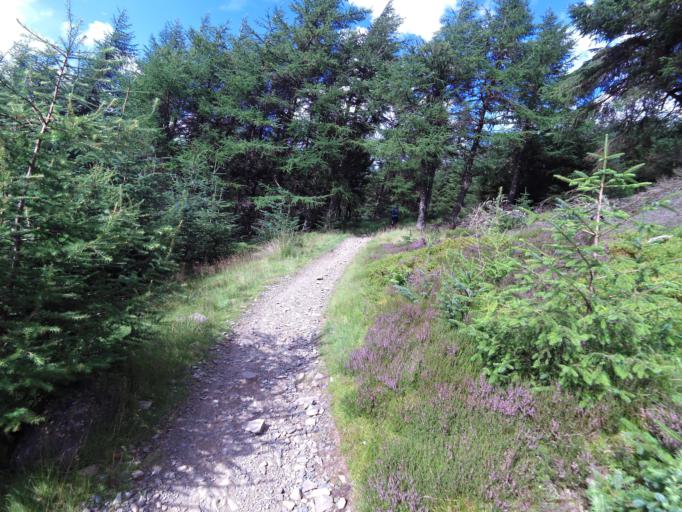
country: GB
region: Scotland
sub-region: The Scottish Borders
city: Peebles
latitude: 55.6711
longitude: -3.1336
